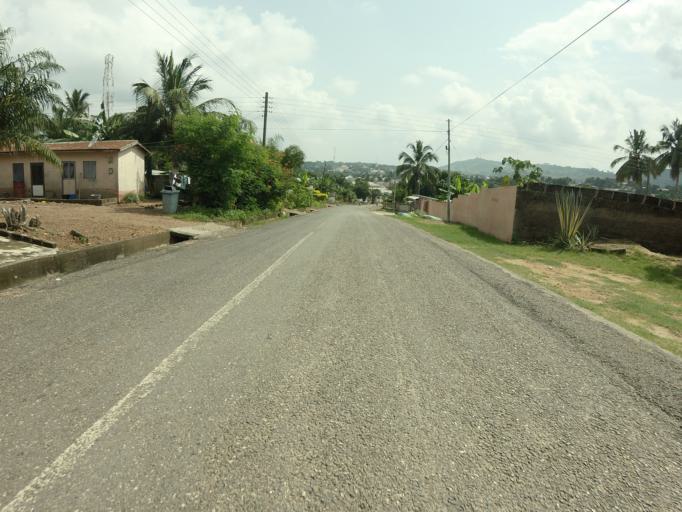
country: GH
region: Volta
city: Ho
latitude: 6.6170
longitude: 0.4795
